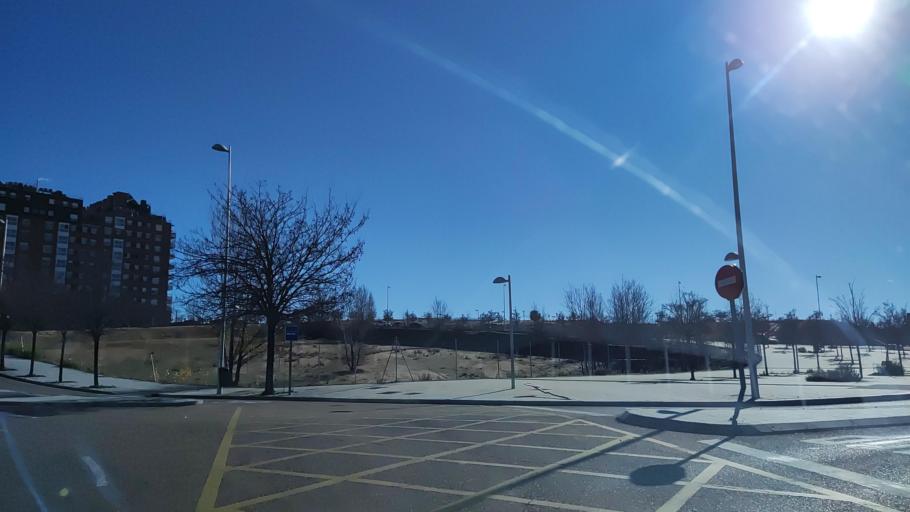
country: ES
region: Madrid
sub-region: Provincia de Madrid
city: Hortaleza
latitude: 40.4939
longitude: -3.6238
